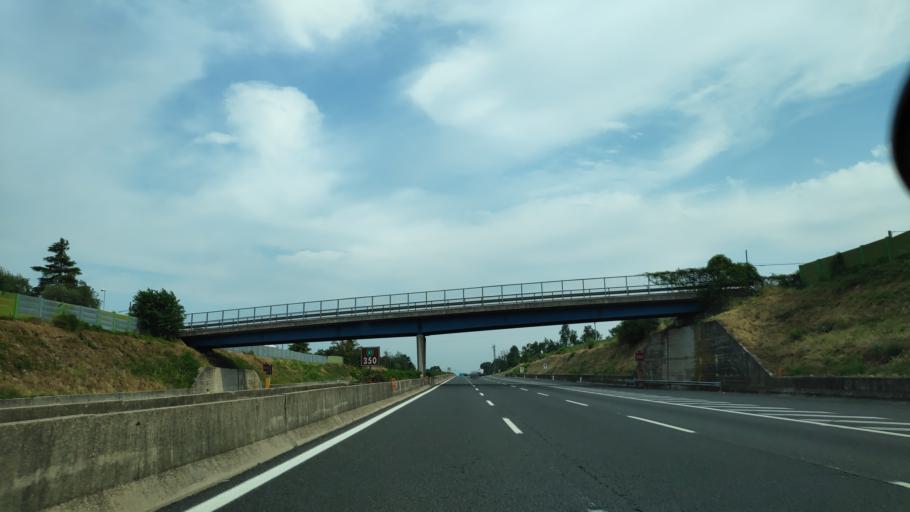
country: IT
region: Latium
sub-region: Citta metropolitana di Roma Capitale
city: Fiano Romano
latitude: 42.1742
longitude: 12.6074
